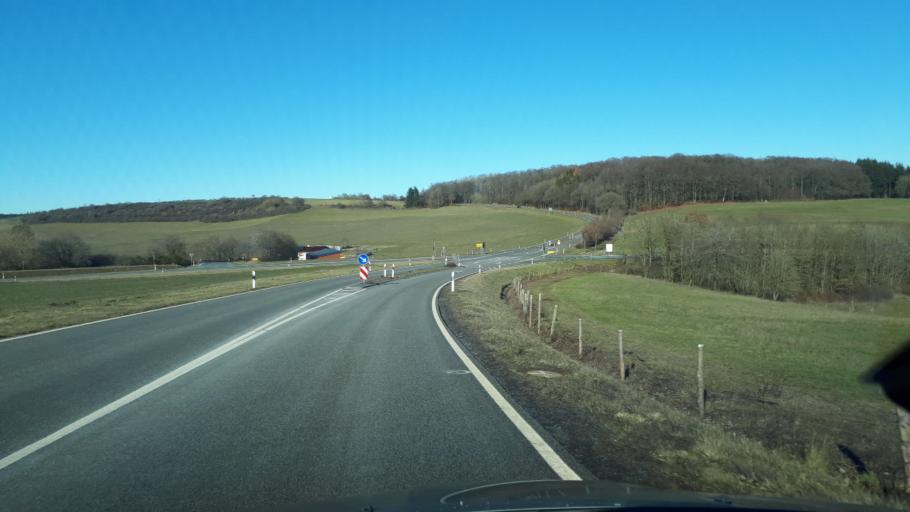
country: DE
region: Rheinland-Pfalz
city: Ellscheid
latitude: 50.1401
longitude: 6.9295
